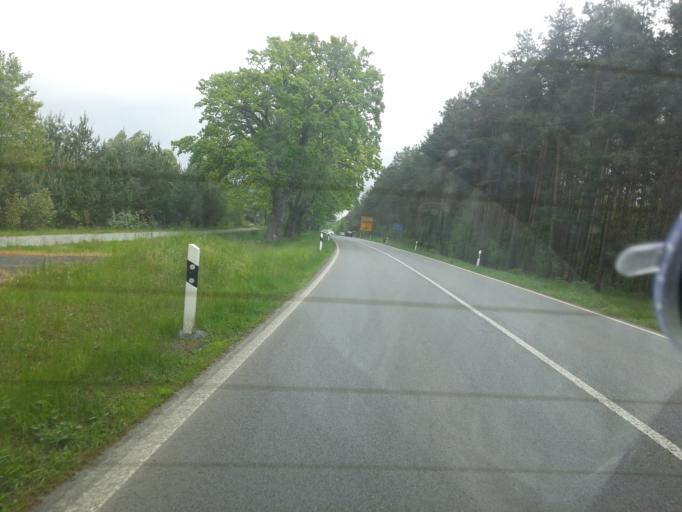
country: DE
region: Mecklenburg-Vorpommern
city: Malchow
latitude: 53.4613
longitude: 12.4194
